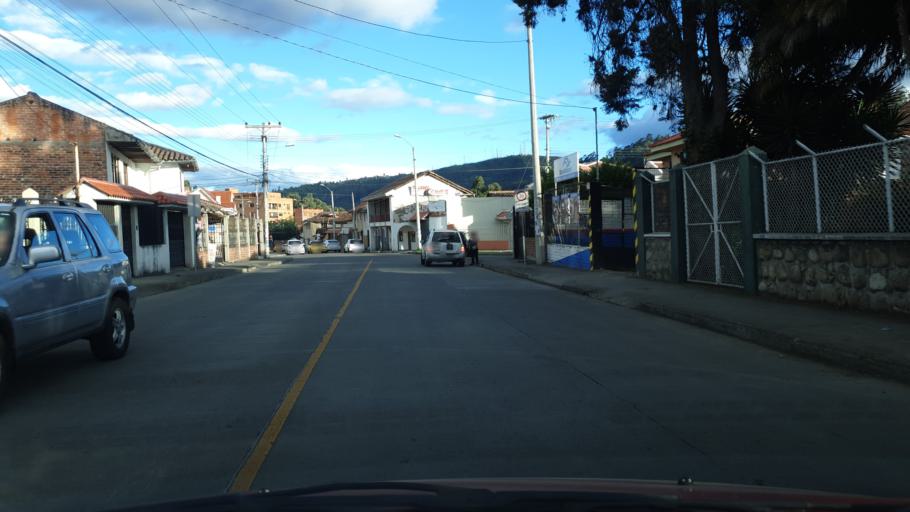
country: EC
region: Azuay
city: Cuenca
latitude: -2.9118
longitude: -79.0166
